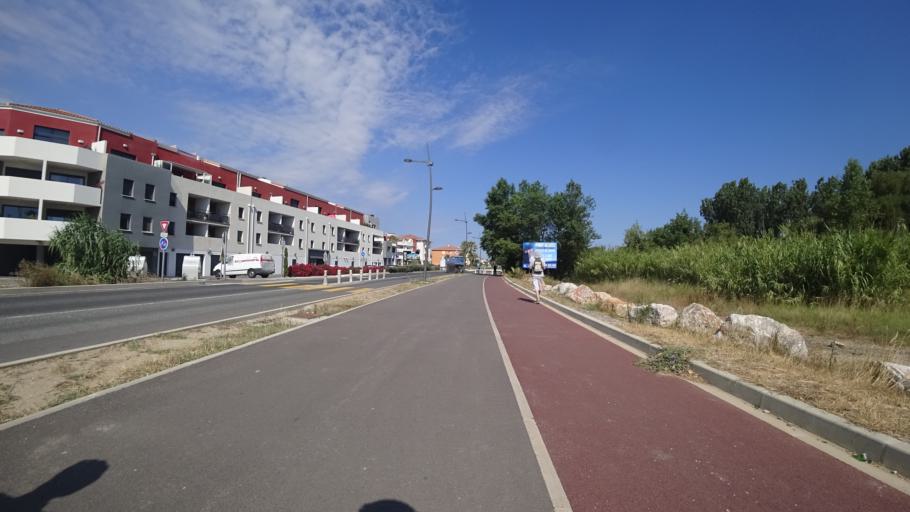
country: FR
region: Languedoc-Roussillon
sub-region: Departement des Pyrenees-Orientales
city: Canet-en-Roussillon
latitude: 42.7030
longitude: 3.0241
